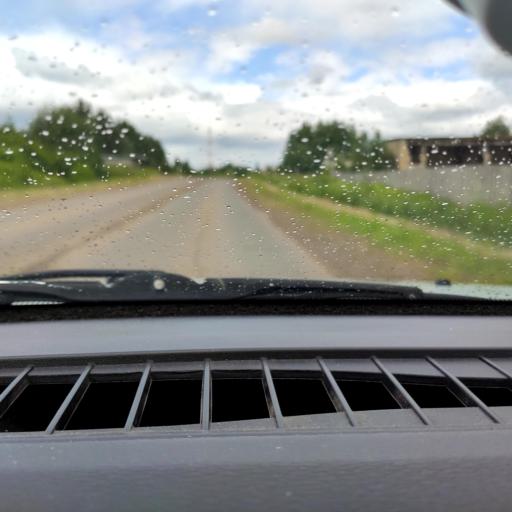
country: RU
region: Perm
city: Uinskoye
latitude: 57.1061
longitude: 56.5336
